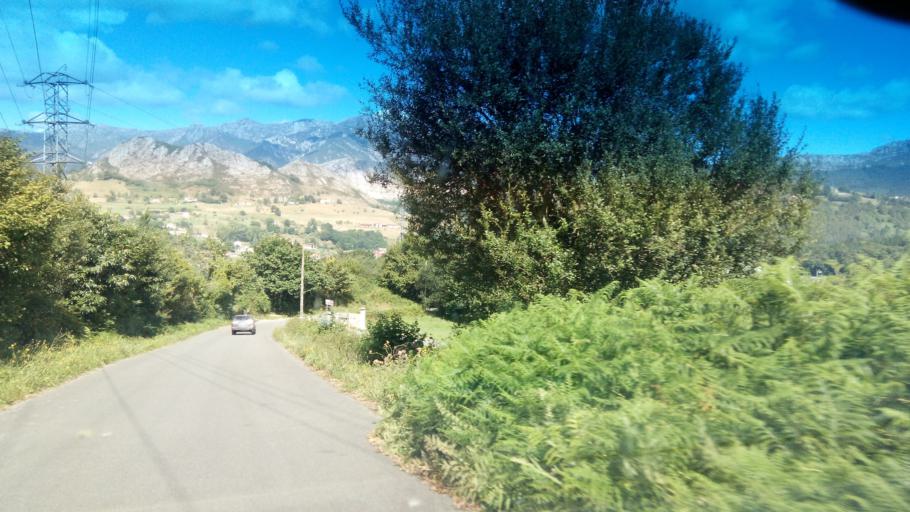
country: ES
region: Asturias
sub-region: Province of Asturias
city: Parres
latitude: 43.3797
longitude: -5.1776
